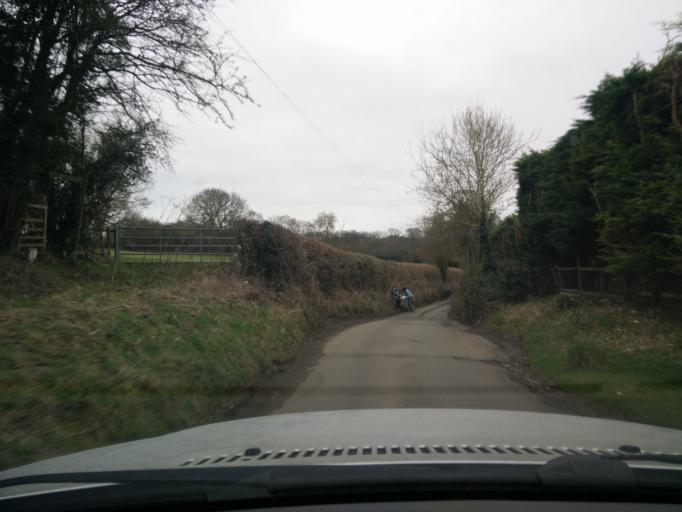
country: GB
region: England
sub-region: Buckinghamshire
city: Beaconsfield
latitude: 51.6409
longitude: -0.6461
